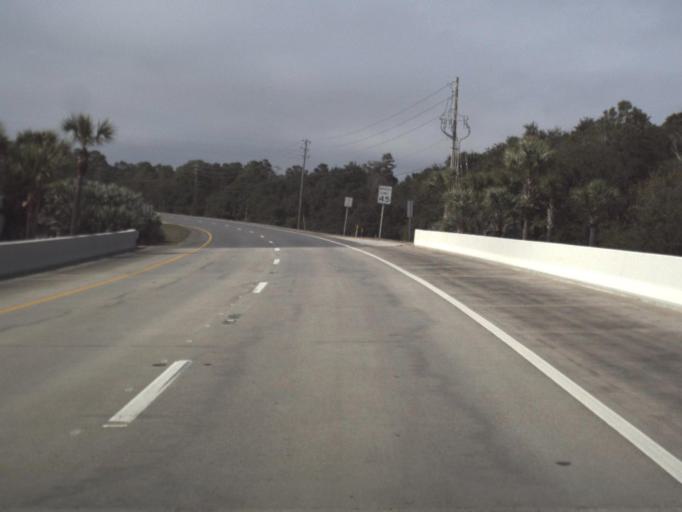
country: US
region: Florida
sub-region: Bay County
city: Laguna Beach
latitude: 30.2752
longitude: -85.9879
